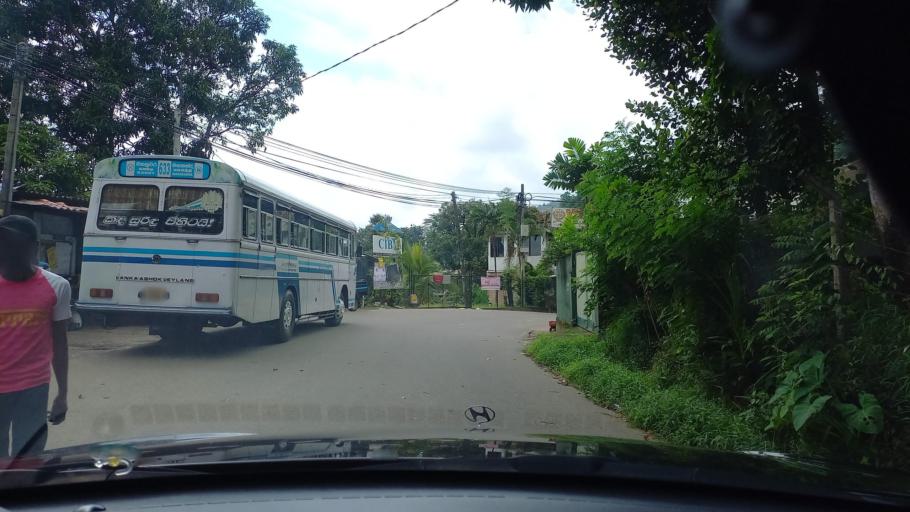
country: LK
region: Central
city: Kandy
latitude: 7.2306
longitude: 80.6052
